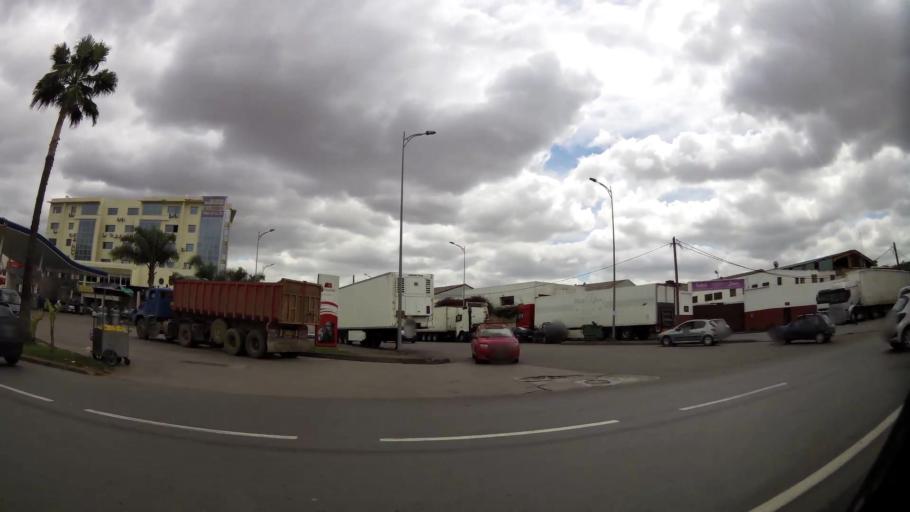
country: MA
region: Grand Casablanca
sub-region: Casablanca
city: Casablanca
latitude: 33.5938
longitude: -7.5457
